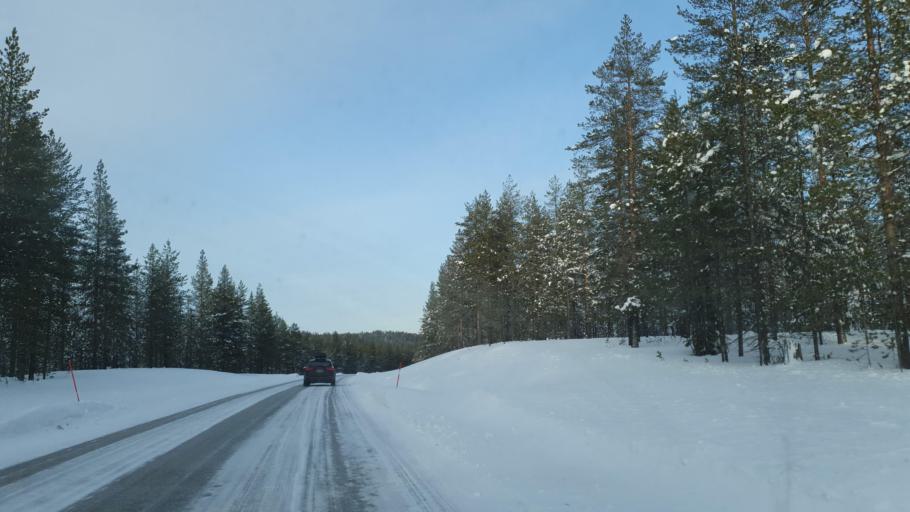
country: FI
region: Lapland
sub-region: Tunturi-Lappi
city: Kolari
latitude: 67.5239
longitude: 23.8973
